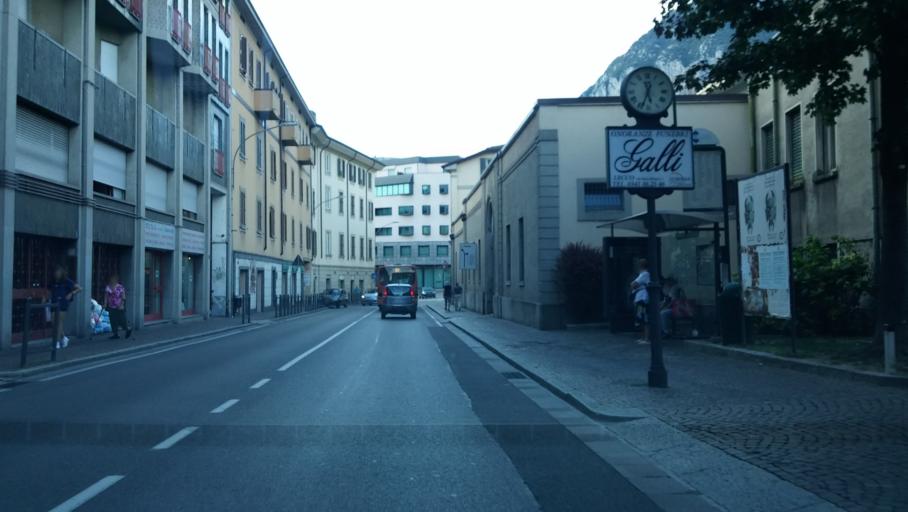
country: IT
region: Lombardy
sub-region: Provincia di Lecco
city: Lecco
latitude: 45.8550
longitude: 9.3939
